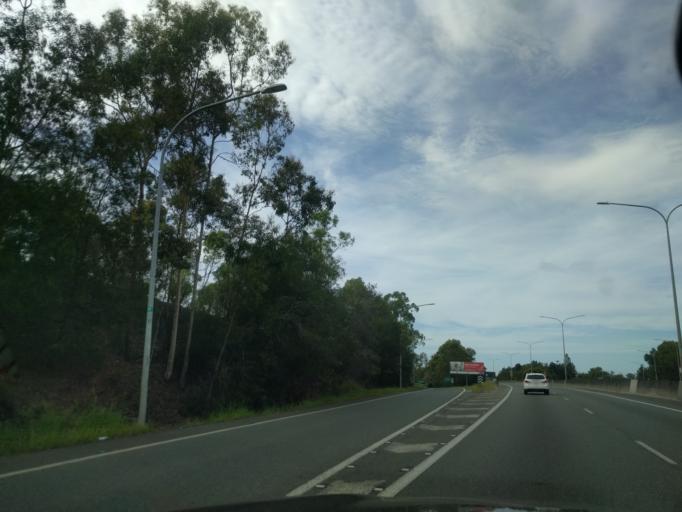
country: AU
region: Queensland
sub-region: Brisbane
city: Seventeen Mile Rocks
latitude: -27.5445
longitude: 152.9425
